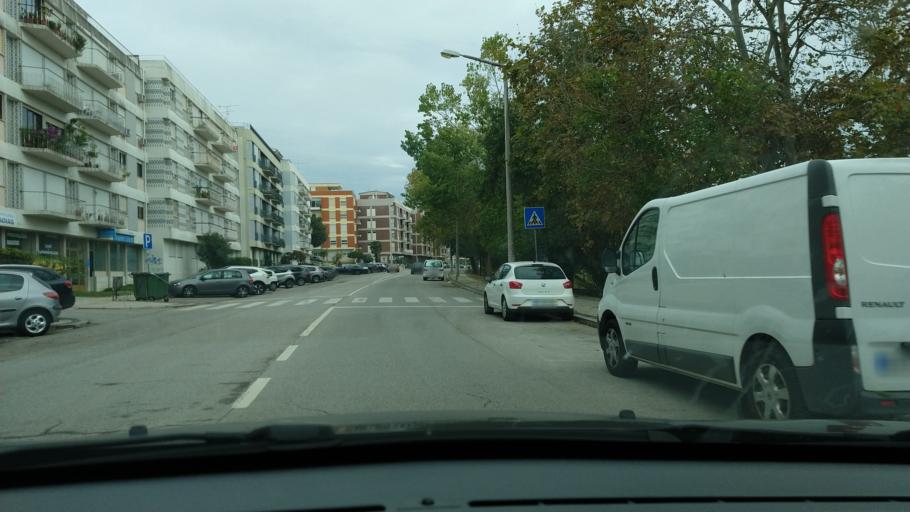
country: PT
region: Coimbra
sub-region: Figueira da Foz
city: Figueira da Foz
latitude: 40.1516
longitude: -8.8620
